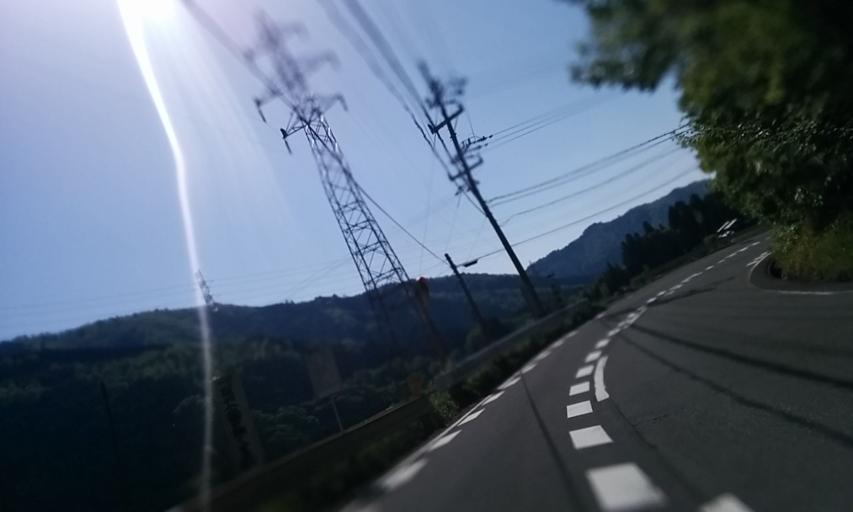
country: JP
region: Kyoto
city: Ayabe
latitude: 35.2592
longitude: 135.4544
